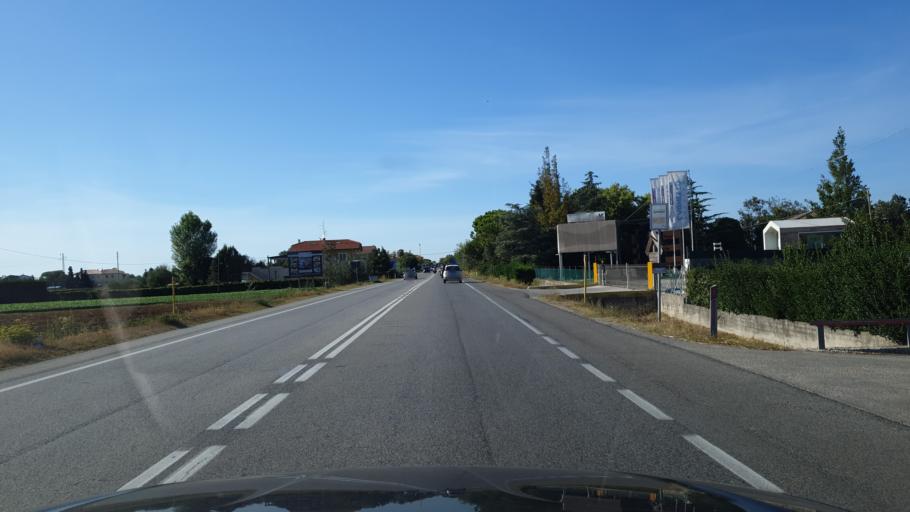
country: IT
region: Emilia-Romagna
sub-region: Provincia di Rimini
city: Santa Giustina
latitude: 44.1000
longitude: 12.4964
